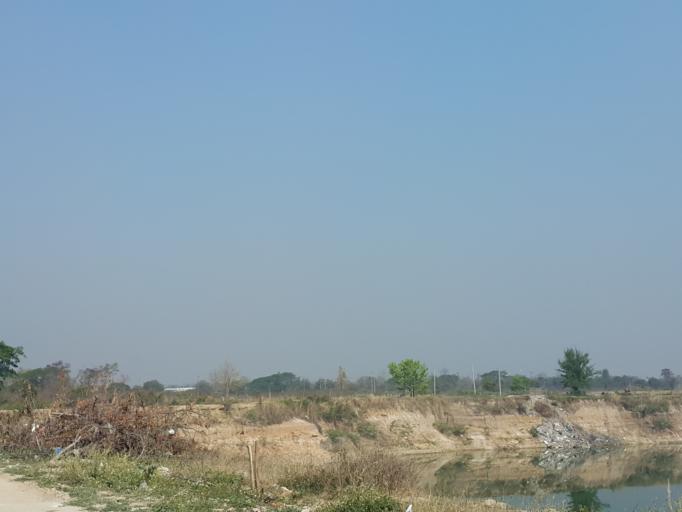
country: TH
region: Chiang Mai
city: San Kamphaeng
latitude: 18.7782
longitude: 99.0782
